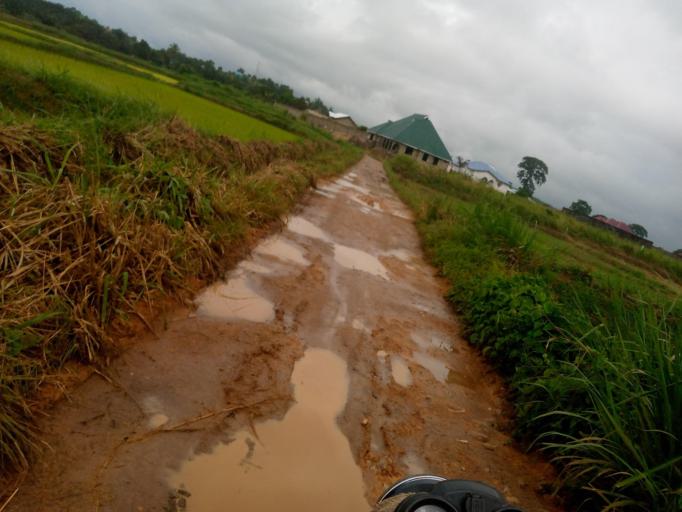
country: SL
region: Eastern Province
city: Kenema
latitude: 7.8525
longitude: -11.2010
